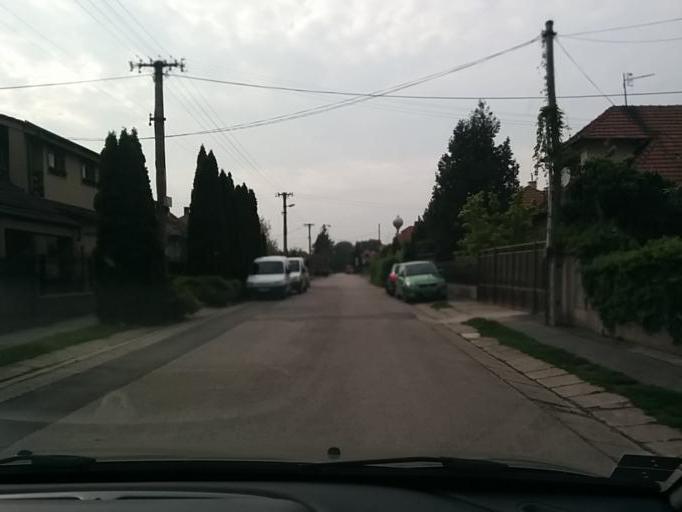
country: SK
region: Trnavsky
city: Sladkovicovo
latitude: 48.2297
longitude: 17.5781
